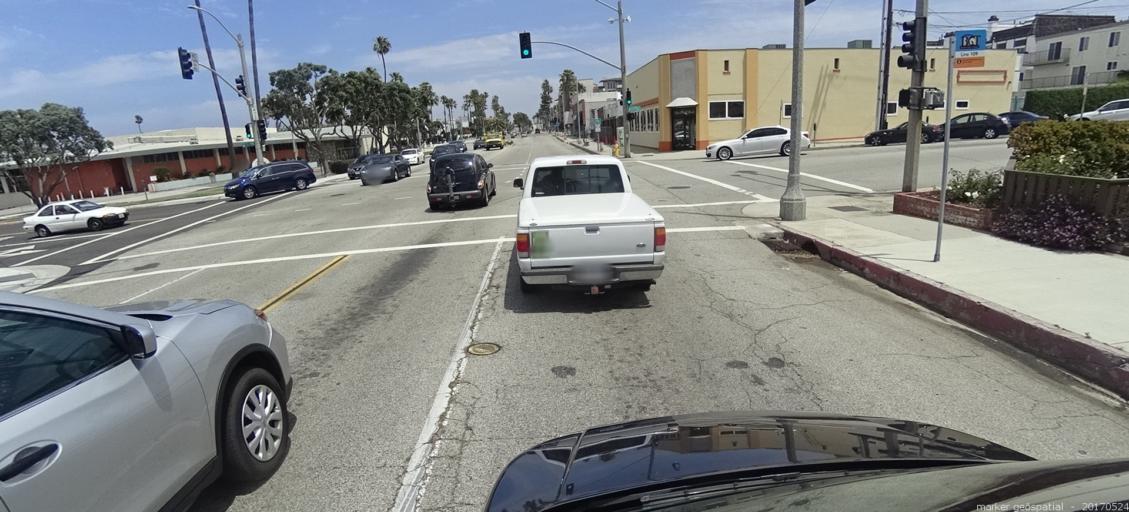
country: US
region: California
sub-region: Los Angeles County
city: Redondo Beach
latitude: 33.8364
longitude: -118.3878
